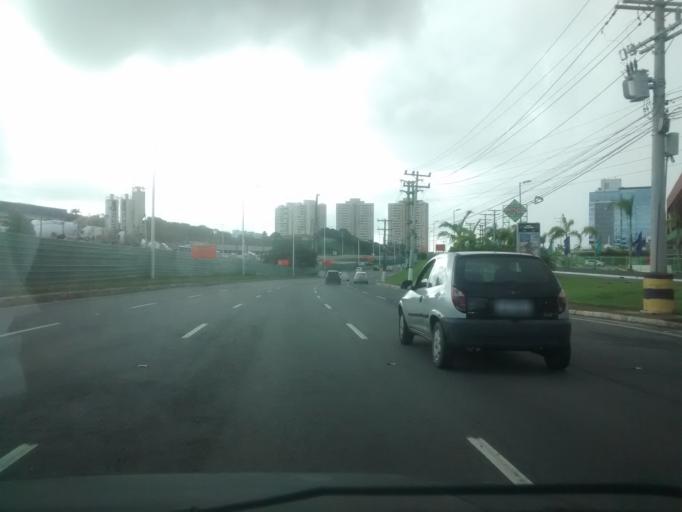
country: BR
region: Bahia
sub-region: Salvador
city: Salvador
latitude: -12.9413
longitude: -38.4177
